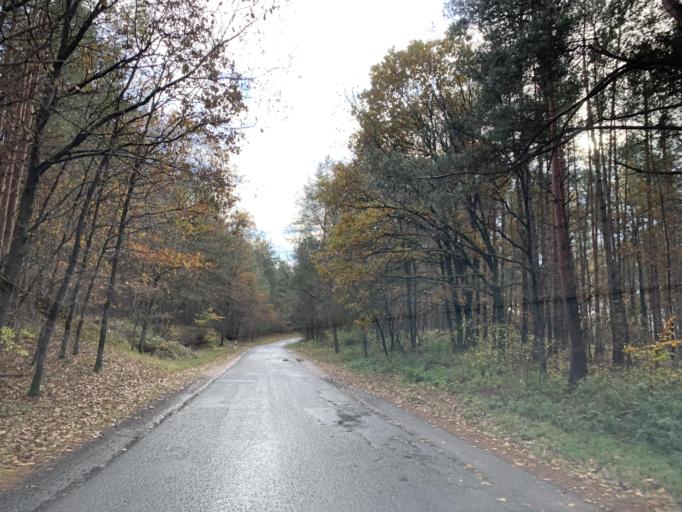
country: DE
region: Mecklenburg-Vorpommern
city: Blankensee
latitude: 53.3927
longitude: 13.2626
